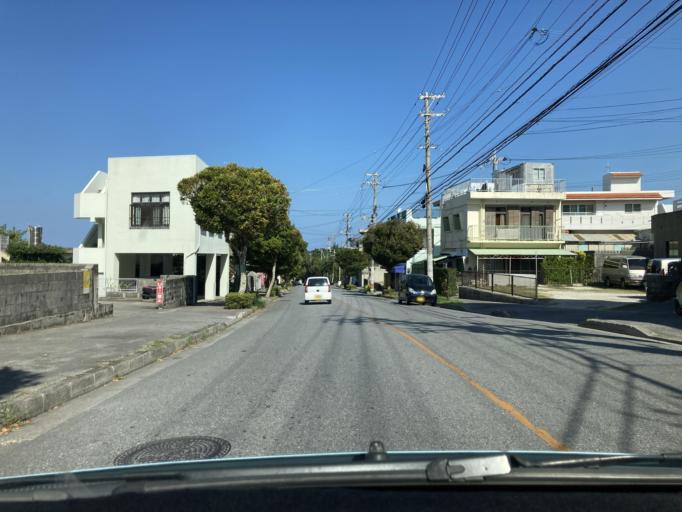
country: JP
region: Okinawa
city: Ginowan
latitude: 26.2501
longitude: 127.7264
